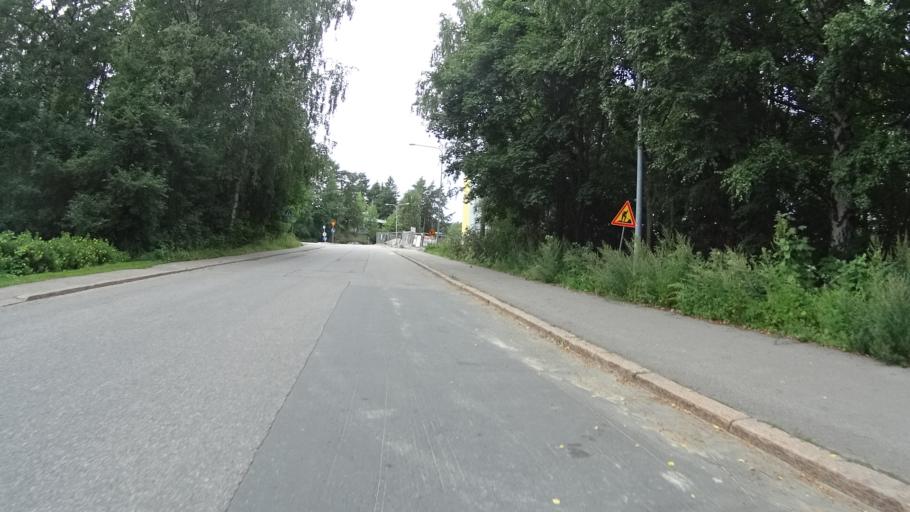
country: FI
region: Uusimaa
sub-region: Helsinki
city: Teekkarikylae
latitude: 60.2367
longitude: 24.8487
